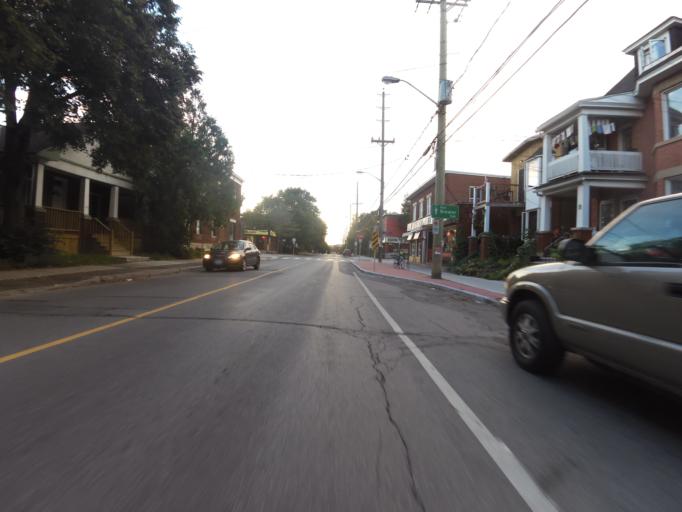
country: CA
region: Ontario
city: Ottawa
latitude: 45.3917
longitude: -75.6894
